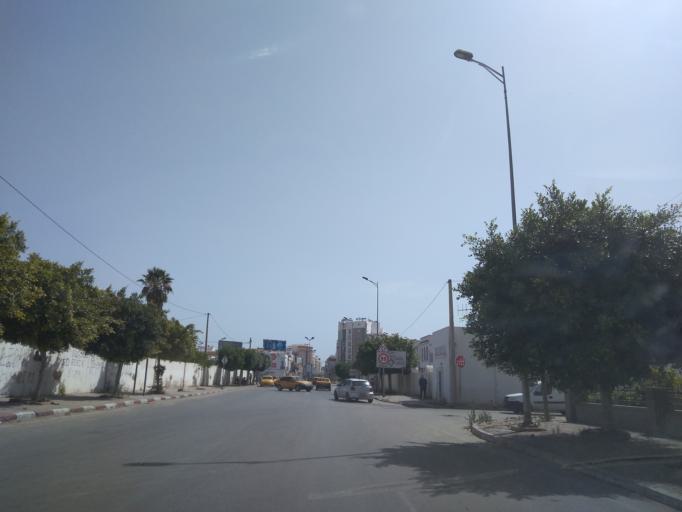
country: TN
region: Safaqis
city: Sfax
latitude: 34.7327
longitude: 10.7499
